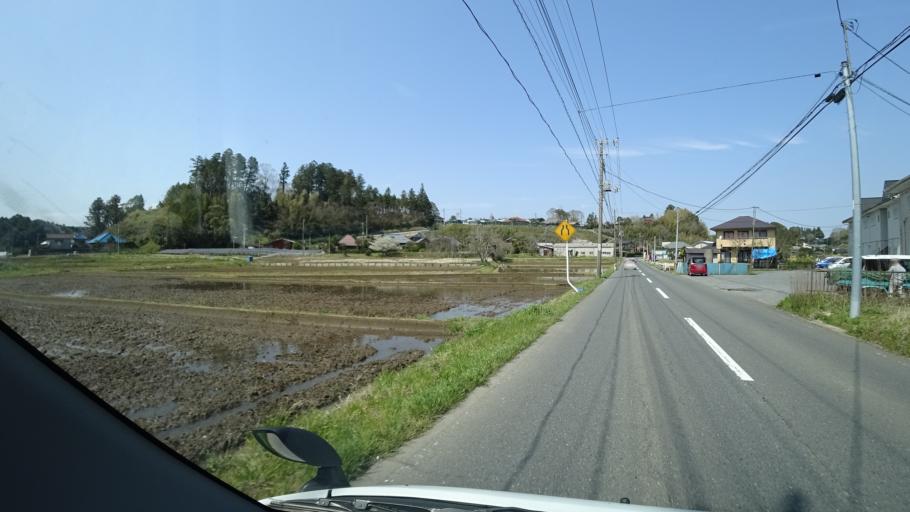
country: JP
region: Chiba
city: Yokaichiba
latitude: 35.7526
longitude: 140.4764
